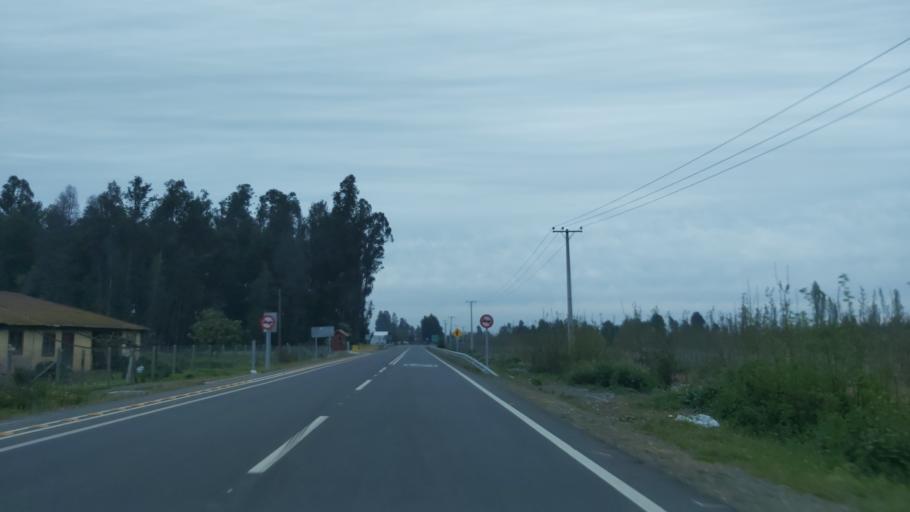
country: CL
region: Maule
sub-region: Provincia de Linares
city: Colbun
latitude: -35.7116
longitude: -71.4815
